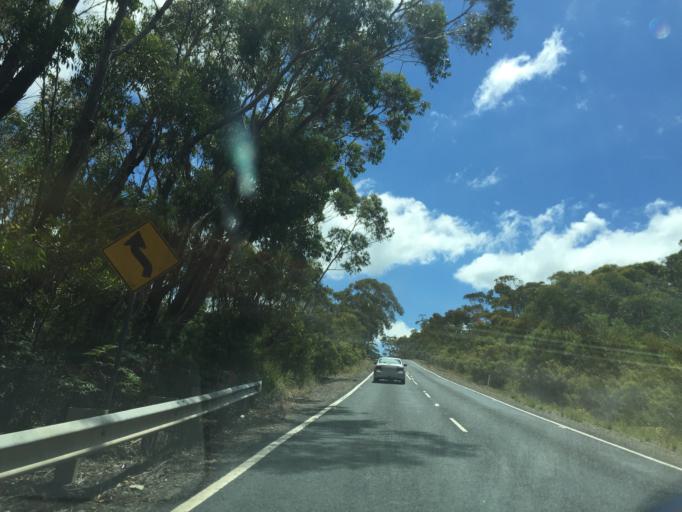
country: AU
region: New South Wales
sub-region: Blue Mountains Municipality
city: Blackheath
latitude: -33.5480
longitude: 150.3953
